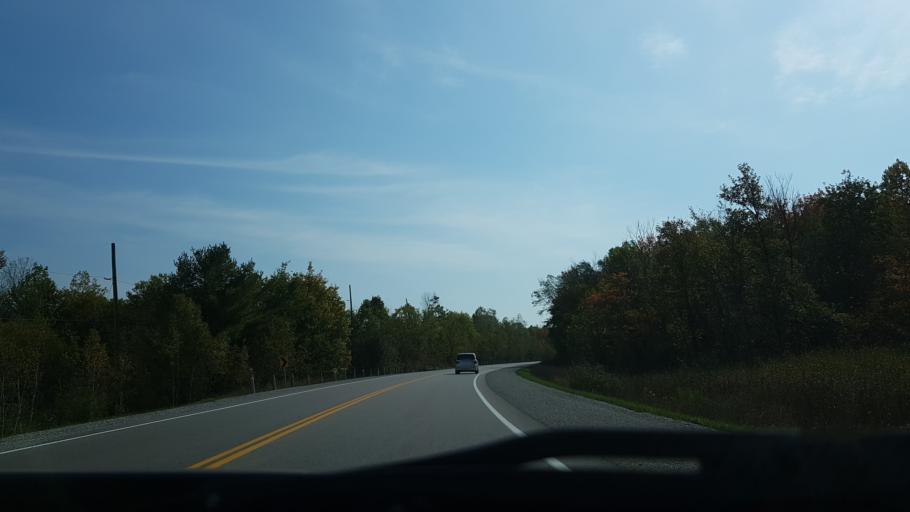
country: CA
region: Ontario
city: Orillia
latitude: 44.7403
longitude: -79.2960
